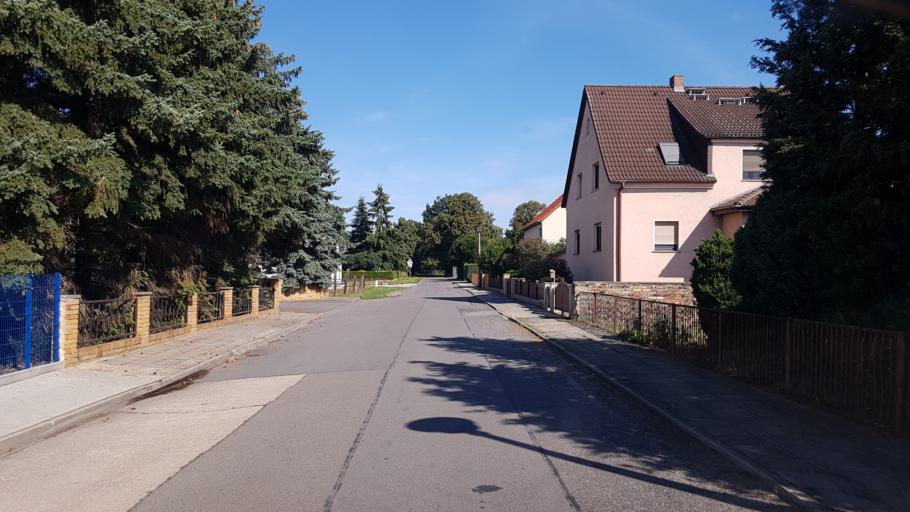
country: DE
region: Brandenburg
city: Plessa
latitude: 51.4683
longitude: 13.6260
